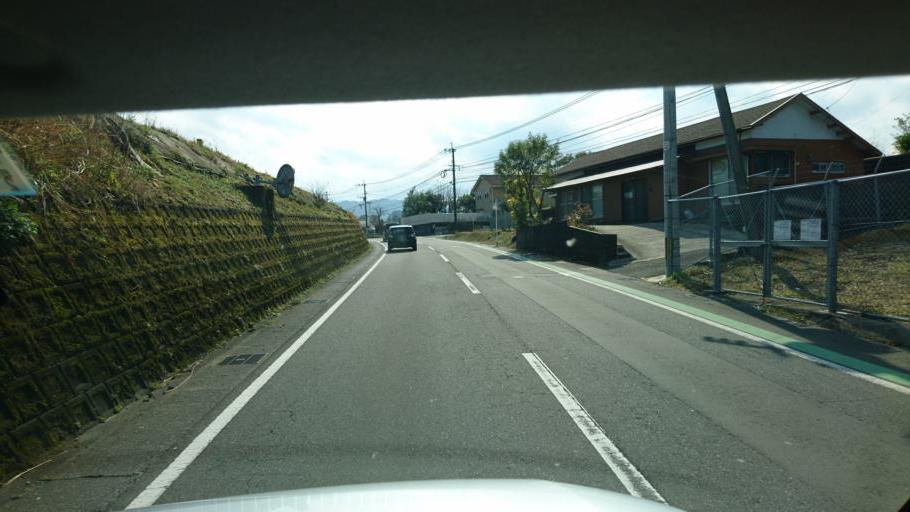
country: JP
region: Miyazaki
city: Miyazaki-shi
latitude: 31.8445
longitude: 131.3936
